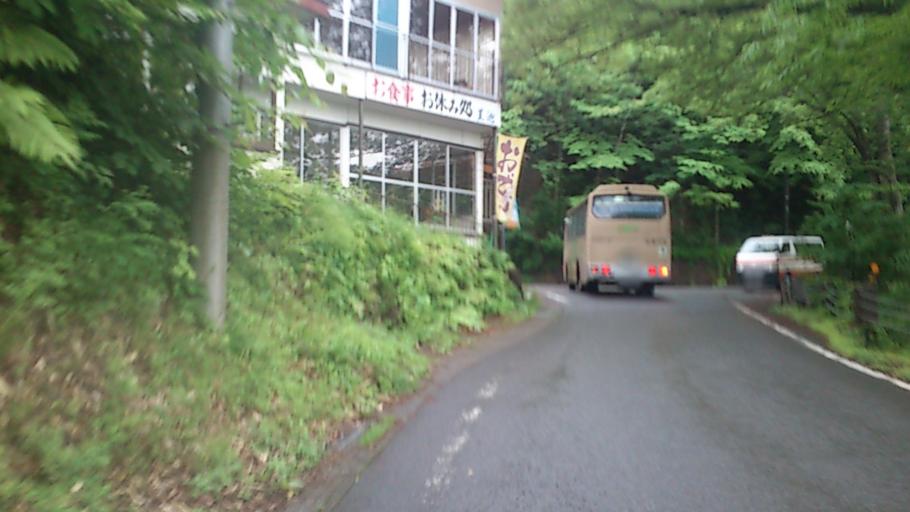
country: JP
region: Akita
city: Noshiromachi
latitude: 40.5634
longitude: 139.9692
